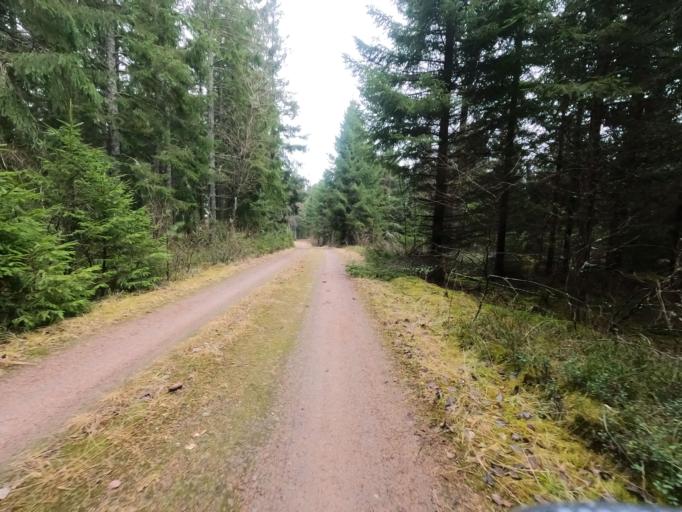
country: SE
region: Kronoberg
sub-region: Markaryds Kommun
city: Stromsnasbruk
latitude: 56.8049
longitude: 13.5692
